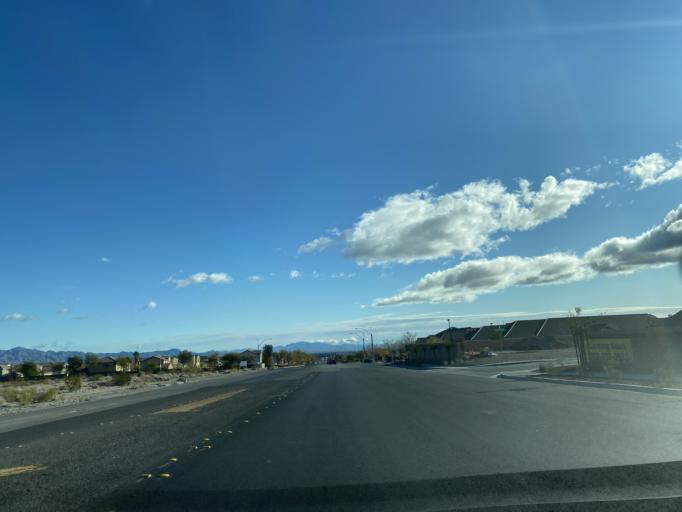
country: US
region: Nevada
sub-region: Clark County
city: Summerlin South
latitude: 36.2772
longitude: -115.2991
